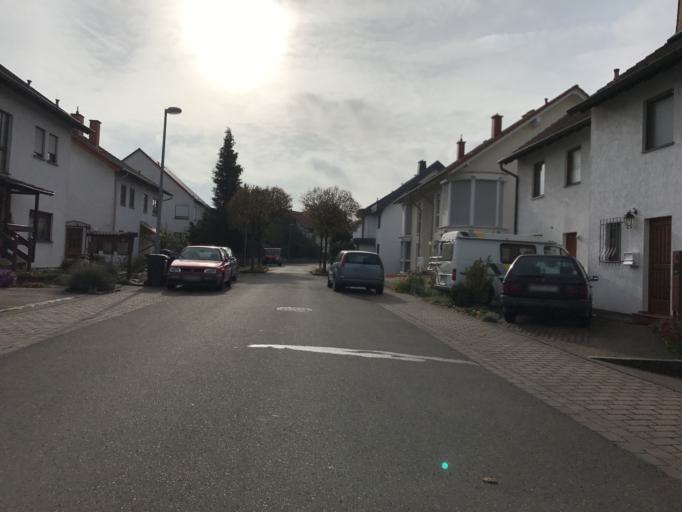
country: DE
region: Rheinland-Pfalz
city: Bubenheim
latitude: 49.9428
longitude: 8.0784
